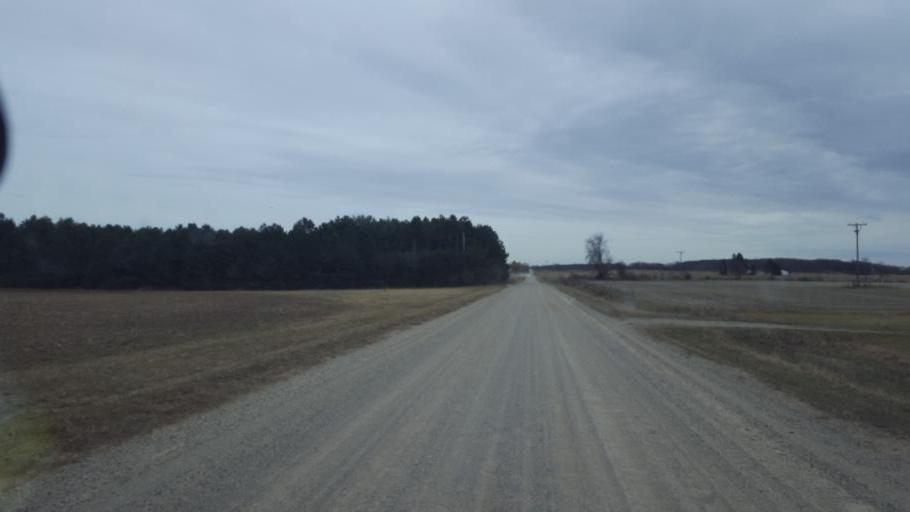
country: US
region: Michigan
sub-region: Montcalm County
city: Edmore
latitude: 43.4513
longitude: -85.0321
